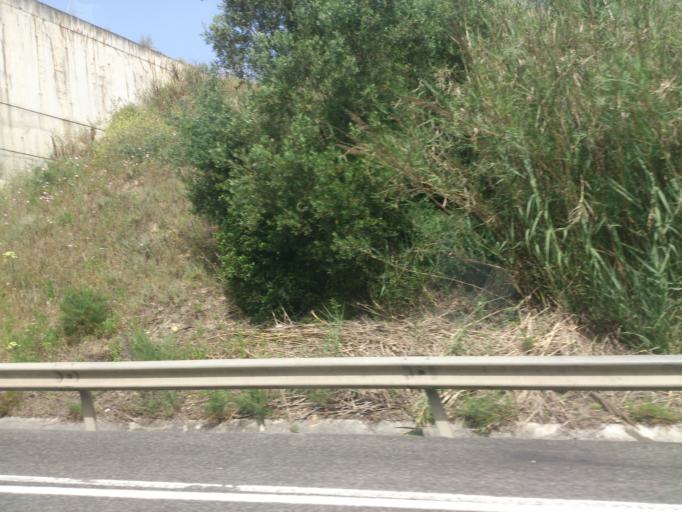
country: PT
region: Lisbon
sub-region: Loures
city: Sacavem
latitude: 38.7920
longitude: -9.1148
